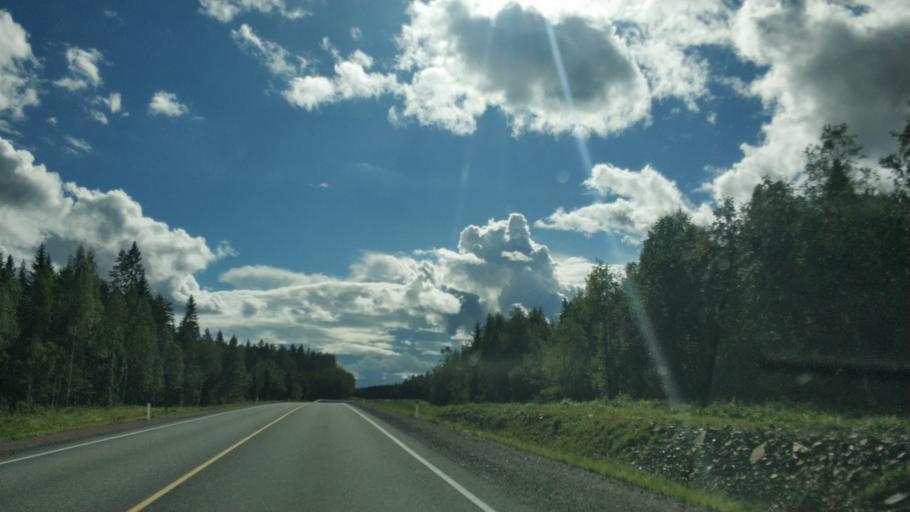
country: RU
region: Republic of Karelia
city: Ruskeala
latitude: 61.8655
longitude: 30.6537
